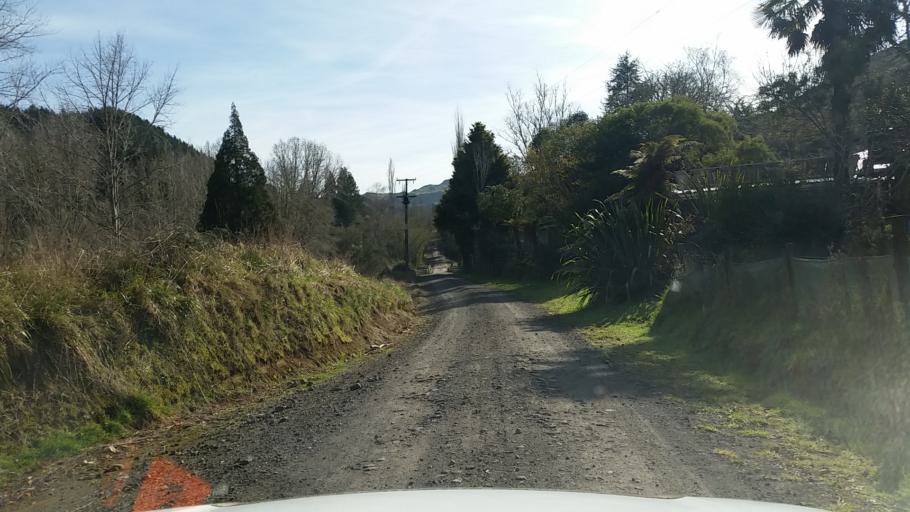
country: NZ
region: Taranaki
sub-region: South Taranaki District
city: Eltham
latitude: -39.3605
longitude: 174.5132
